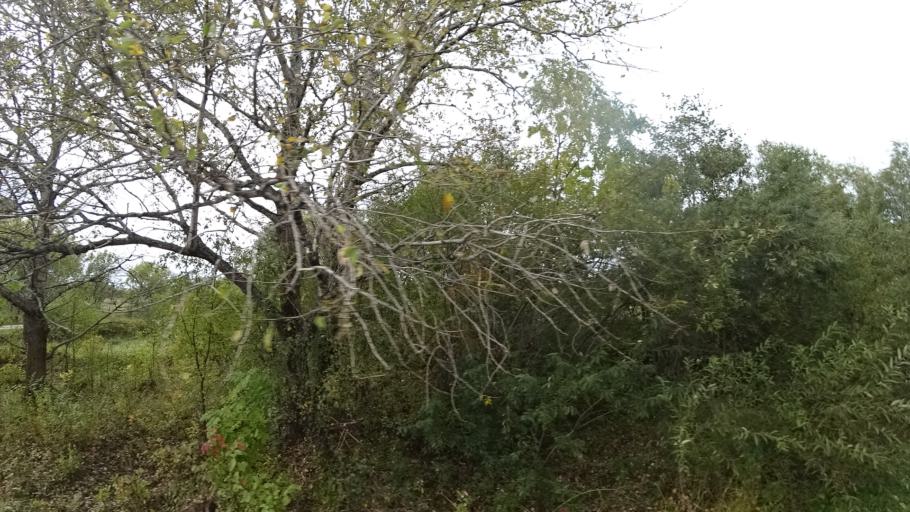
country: RU
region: Amur
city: Arkhara
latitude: 49.3101
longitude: 130.1795
